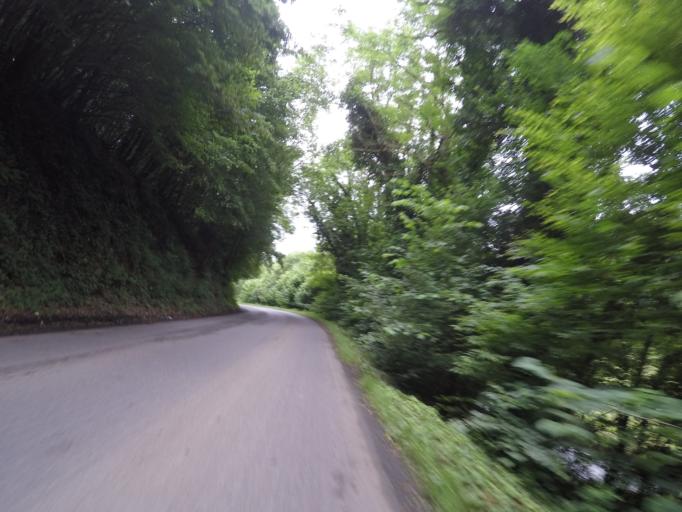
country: BE
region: Wallonia
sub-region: Province de Namur
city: Yvoir
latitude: 50.3428
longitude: 4.9286
